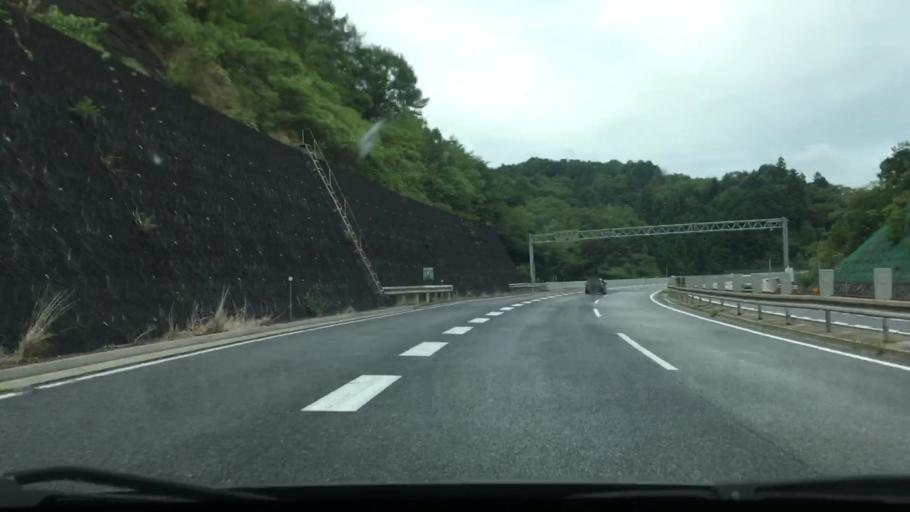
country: JP
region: Hiroshima
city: Hiroshima-shi
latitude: 34.5186
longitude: 132.4270
